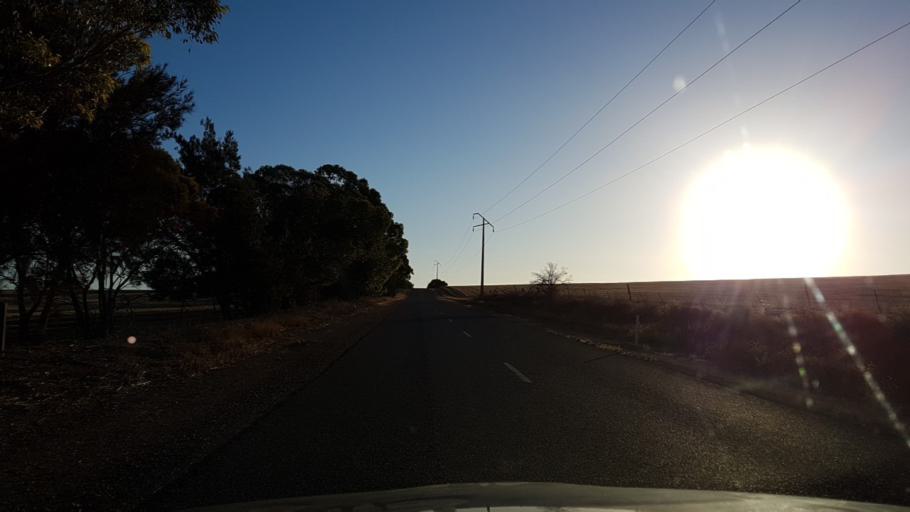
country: AU
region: South Australia
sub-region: Clare and Gilbert Valleys
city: Clare
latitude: -34.0205
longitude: 138.7018
